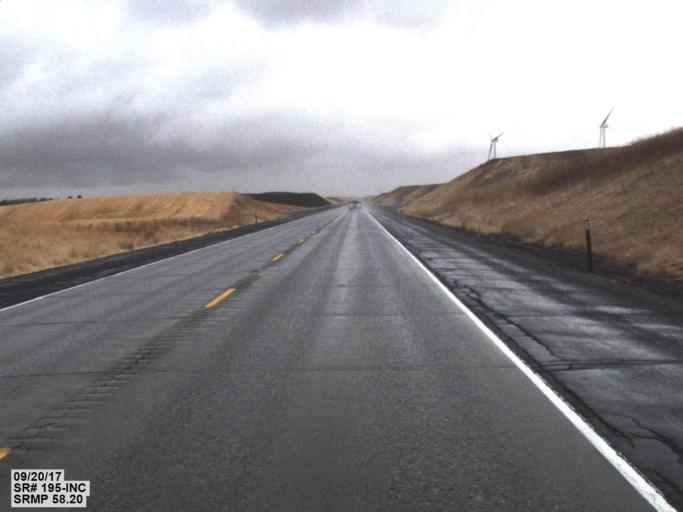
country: US
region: Washington
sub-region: Whitman County
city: Colfax
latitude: 47.1488
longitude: -117.3792
